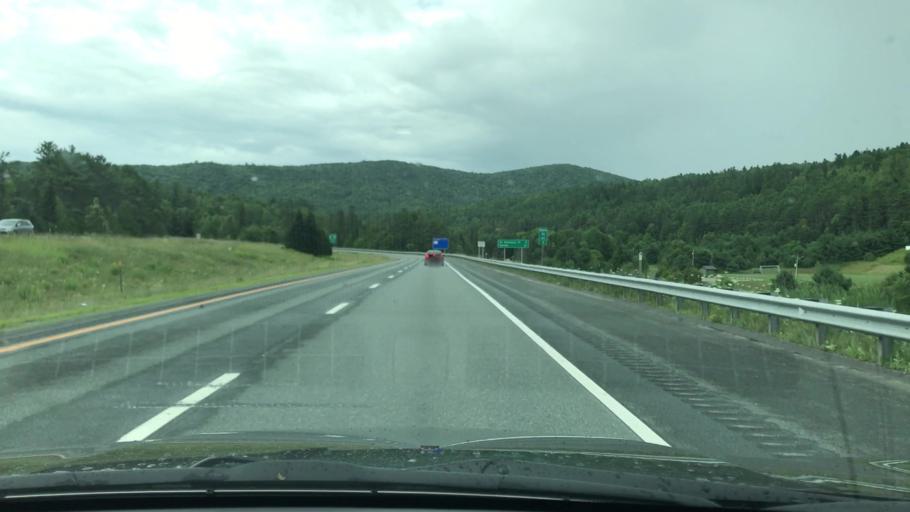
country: US
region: New Hampshire
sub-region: Grafton County
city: Littleton
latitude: 44.3188
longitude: -71.7968
